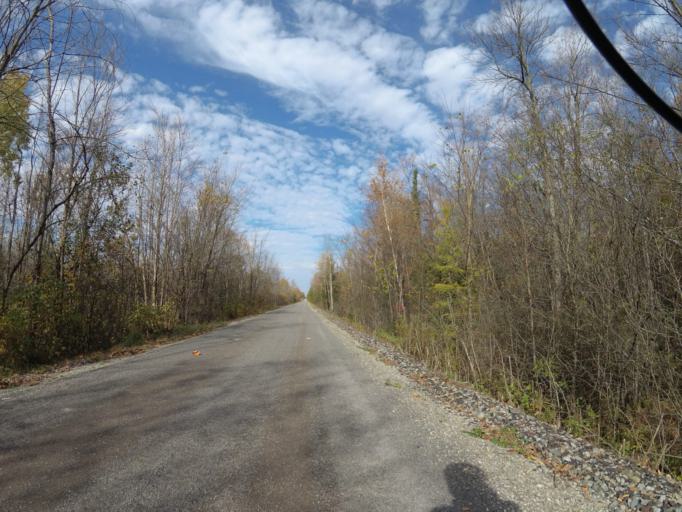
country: CA
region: Ontario
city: Carleton Place
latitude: 45.0536
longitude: -76.0906
